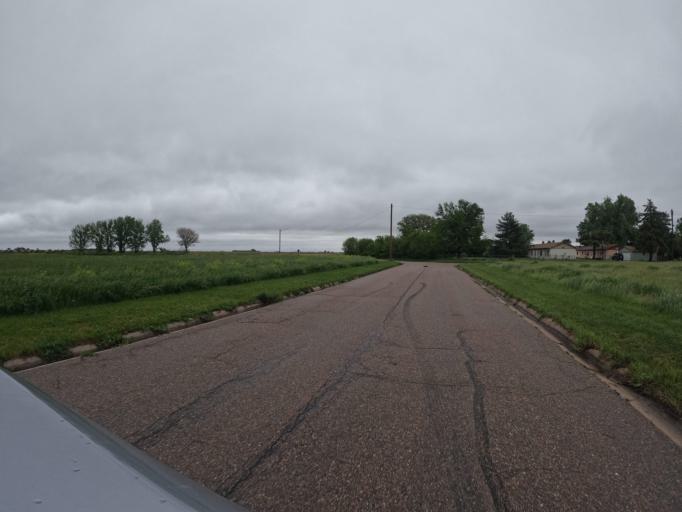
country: US
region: Nebraska
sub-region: Clay County
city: Harvard
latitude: 40.6285
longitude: -98.0909
